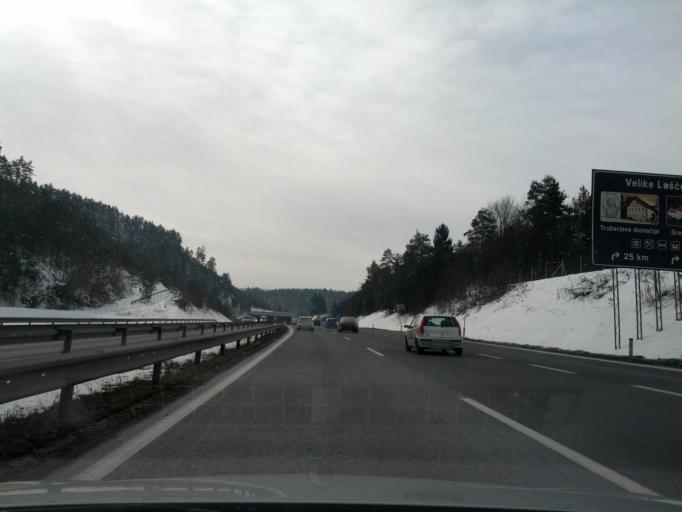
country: SI
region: Skofljica
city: Lavrica
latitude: 46.0348
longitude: 14.5719
